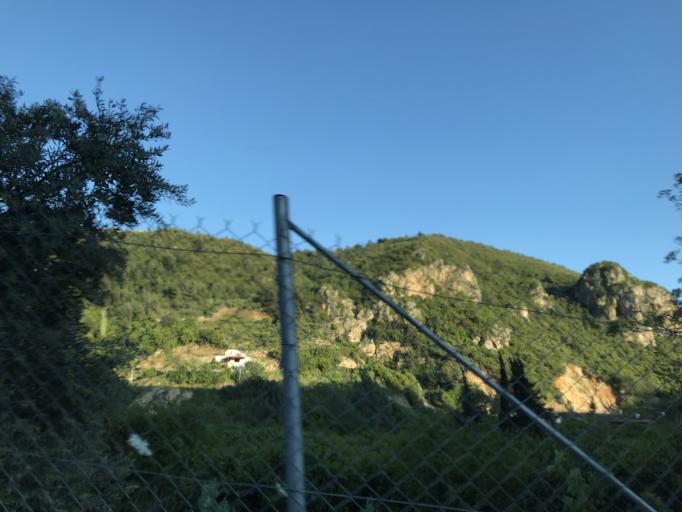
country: TR
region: Hatay
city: Buyukcat
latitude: 36.0811
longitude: 36.0479
